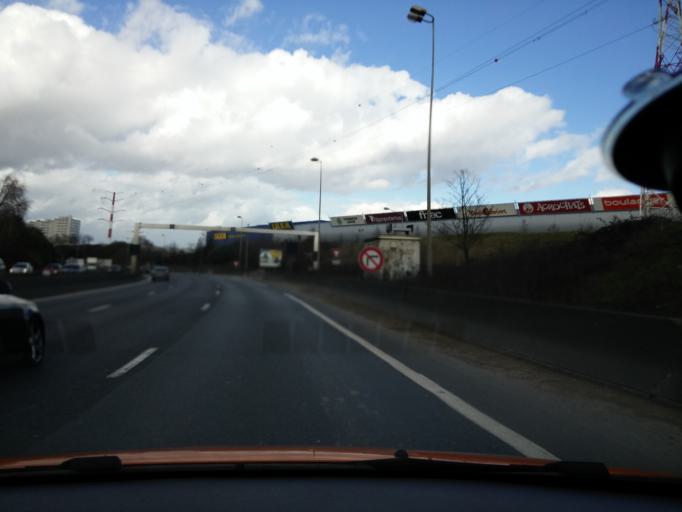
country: FR
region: Ile-de-France
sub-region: Departement du Val-de-Marne
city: Orly
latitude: 48.7570
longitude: 2.3841
